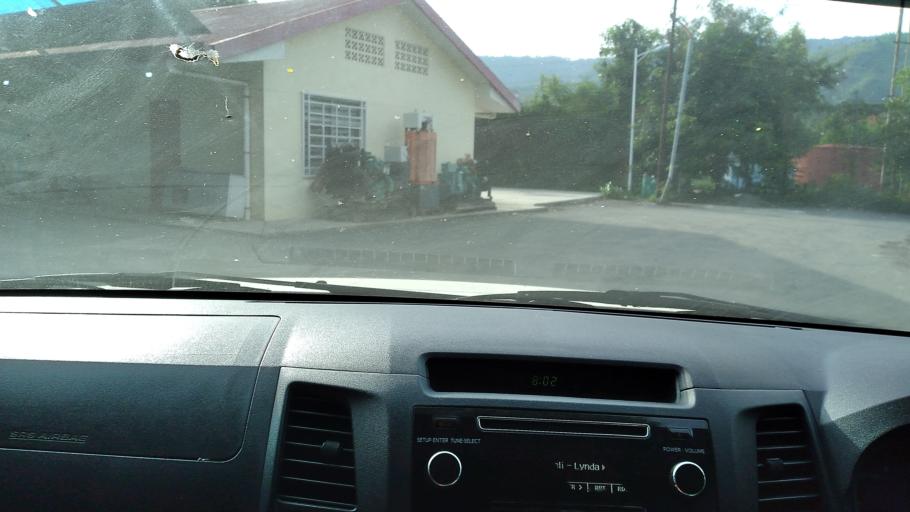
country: TL
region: Dili
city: Dili
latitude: -8.5581
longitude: 125.5744
